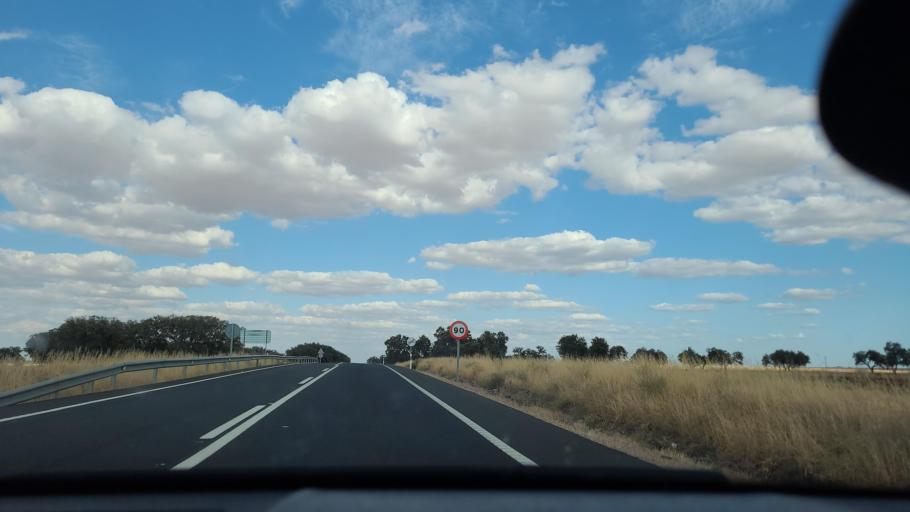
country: ES
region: Extremadura
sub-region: Provincia de Badajoz
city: Casas de Reina
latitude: 38.2499
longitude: -5.9424
